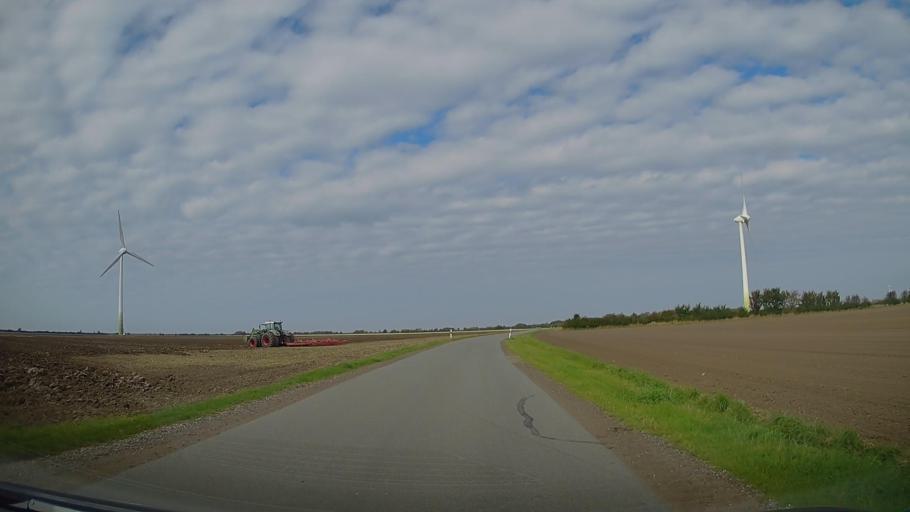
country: DE
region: Schleswig-Holstein
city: Grossenbrode
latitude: 54.5112
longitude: 11.0550
